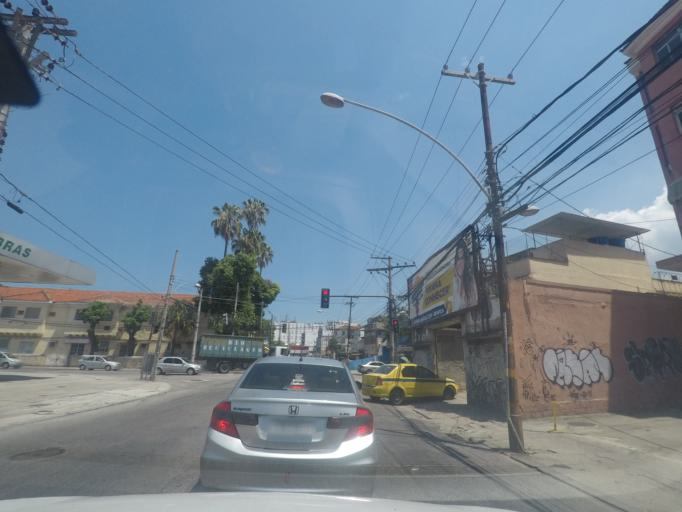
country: BR
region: Rio de Janeiro
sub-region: Rio De Janeiro
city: Rio de Janeiro
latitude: -22.8512
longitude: -43.2644
